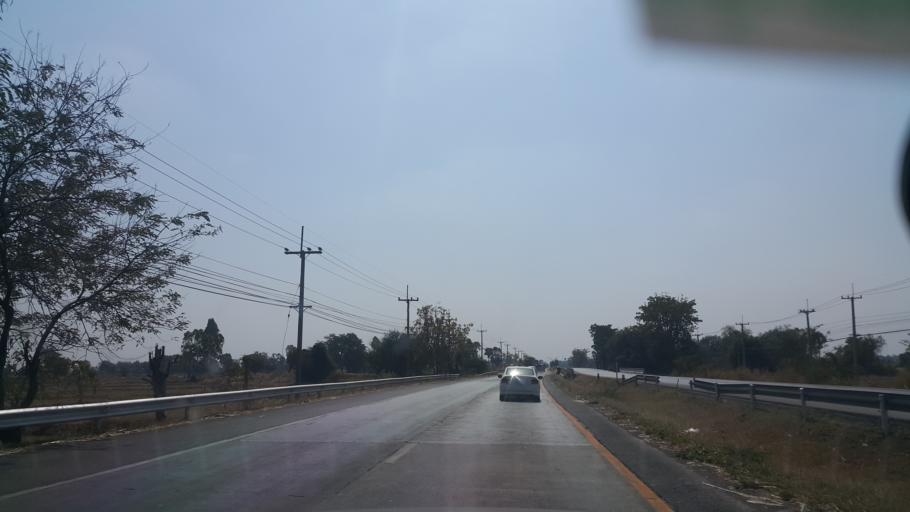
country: TH
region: Nakhon Ratchasima
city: Sida
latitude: 15.5199
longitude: 102.5407
